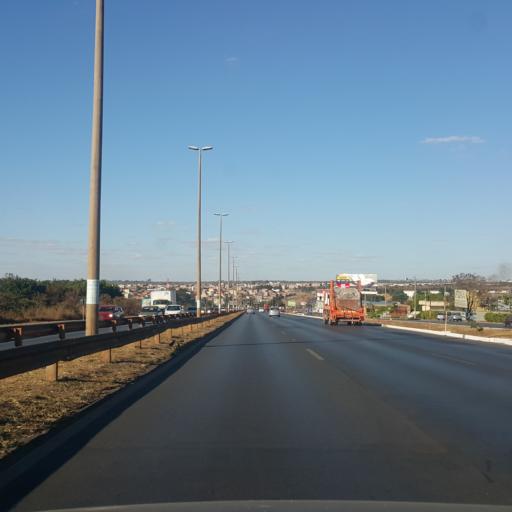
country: BR
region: Federal District
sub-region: Brasilia
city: Brasilia
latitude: -15.7883
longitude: -48.0145
